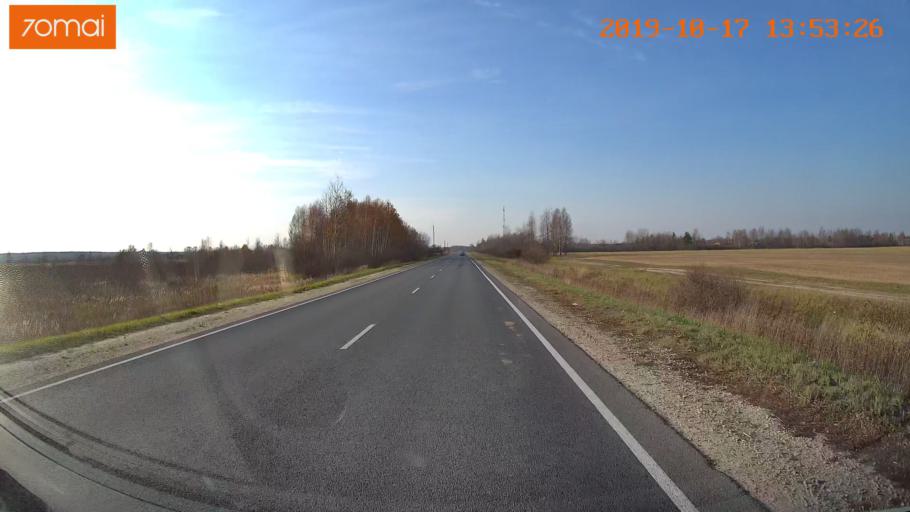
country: RU
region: Rjazan
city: Spas-Klepiki
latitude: 55.1424
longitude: 40.3412
